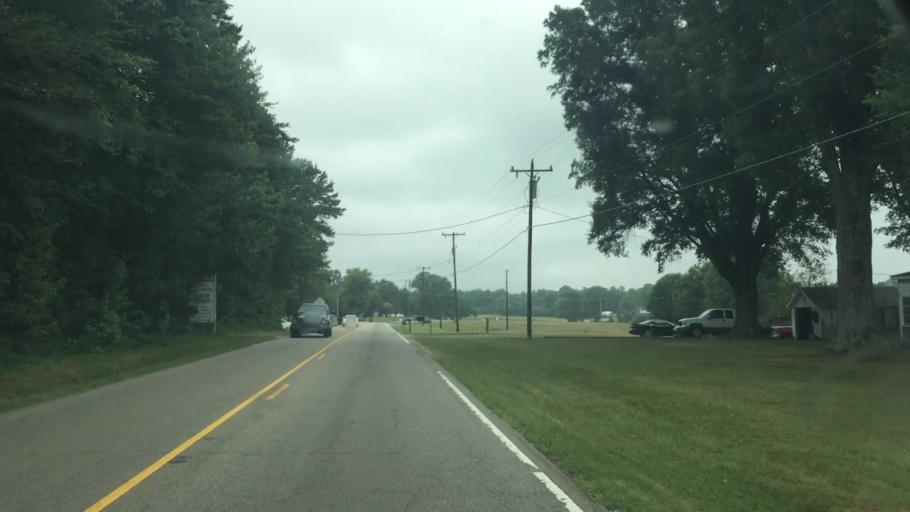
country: US
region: North Carolina
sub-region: Gaston County
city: Davidson
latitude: 35.4937
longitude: -80.7680
